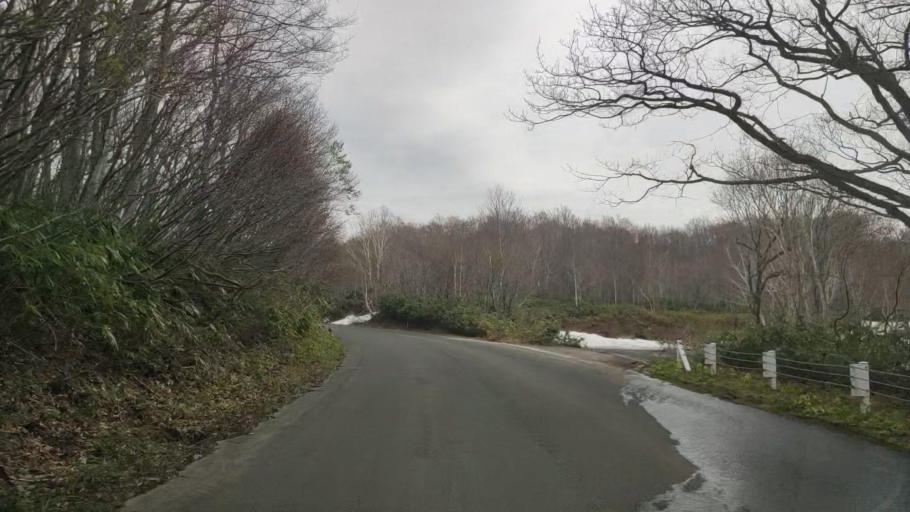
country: JP
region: Aomori
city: Aomori Shi
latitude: 40.6904
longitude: 140.9136
